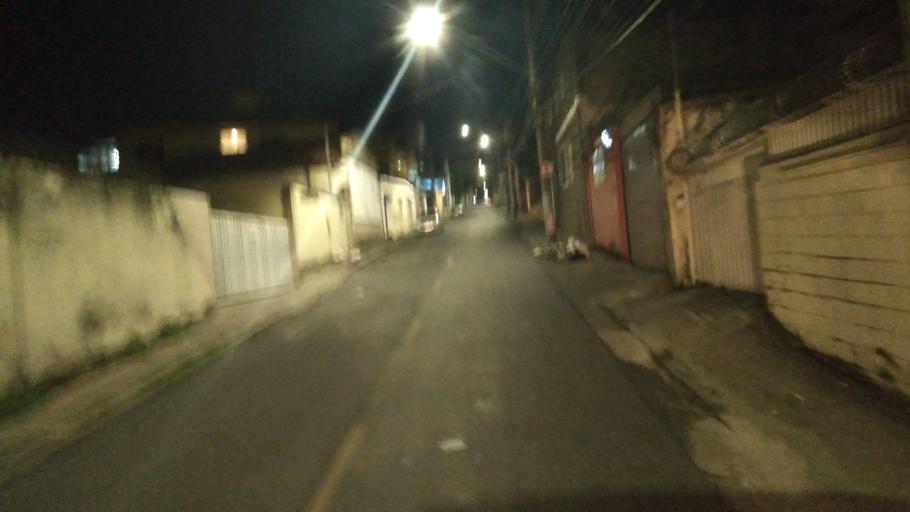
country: BR
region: Minas Gerais
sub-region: Belo Horizonte
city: Belo Horizonte
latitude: -19.9102
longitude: -43.9447
